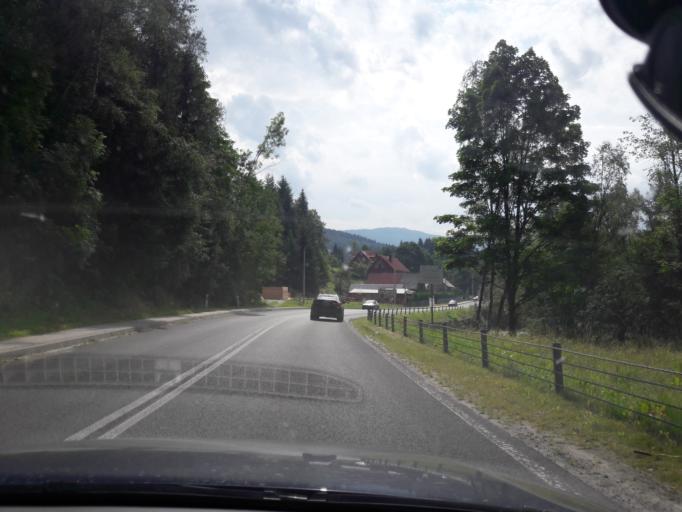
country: PL
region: Lesser Poland Voivodeship
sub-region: Powiat suski
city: Zawoja
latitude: 49.6461
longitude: 19.5438
